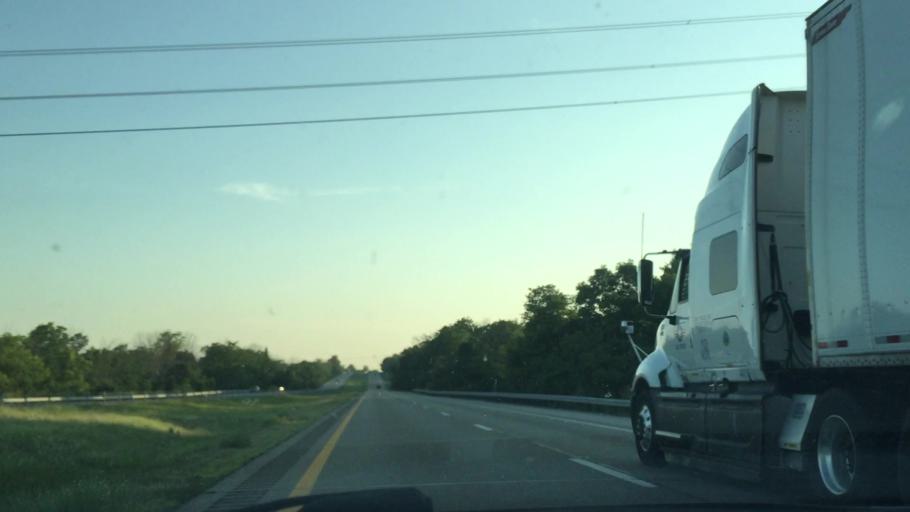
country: US
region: Indiana
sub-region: Switzerland County
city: Vevay
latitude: 38.6731
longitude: -85.0124
